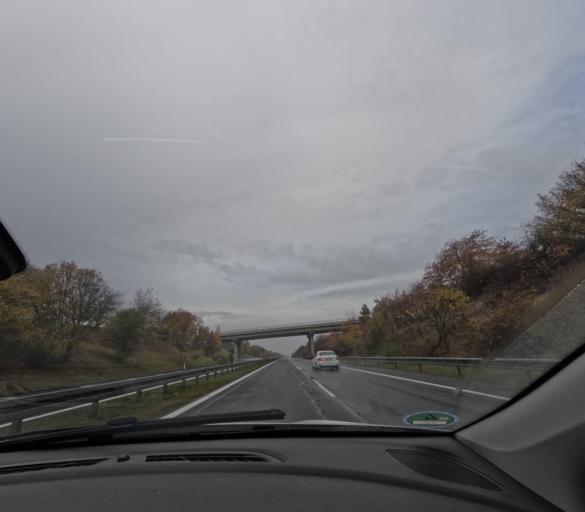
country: CZ
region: Central Bohemia
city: Nove Straseci
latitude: 50.1606
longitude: 13.9265
